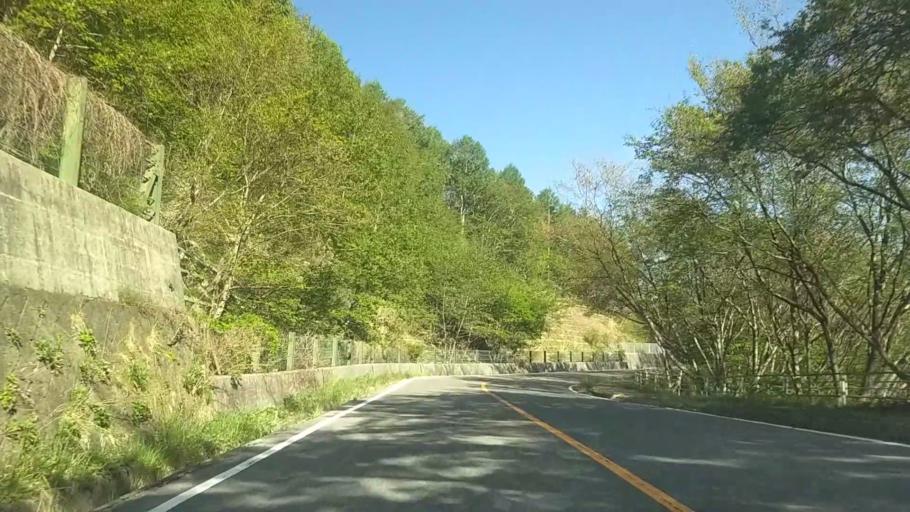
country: JP
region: Yamanashi
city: Nirasaki
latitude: 35.9033
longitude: 138.3824
